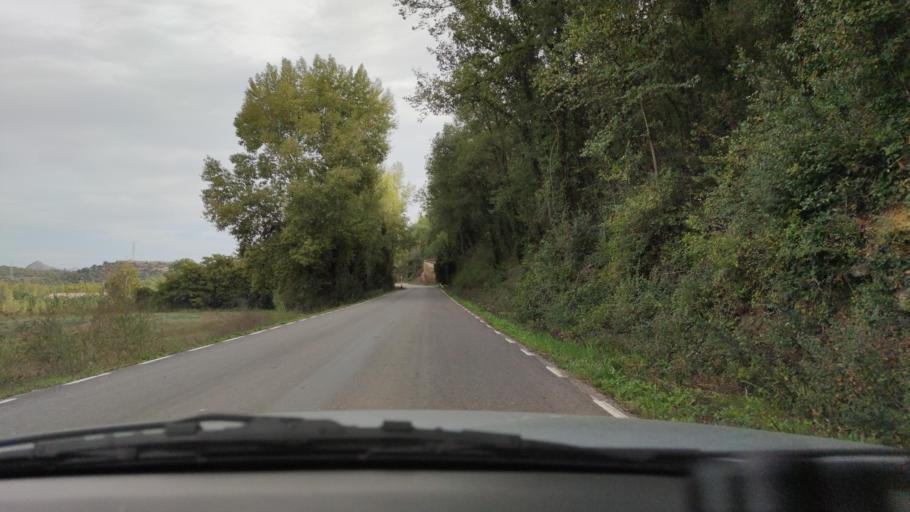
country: ES
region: Catalonia
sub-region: Provincia de Lleida
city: Artesa de Segre
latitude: 41.9171
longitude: 1.0797
